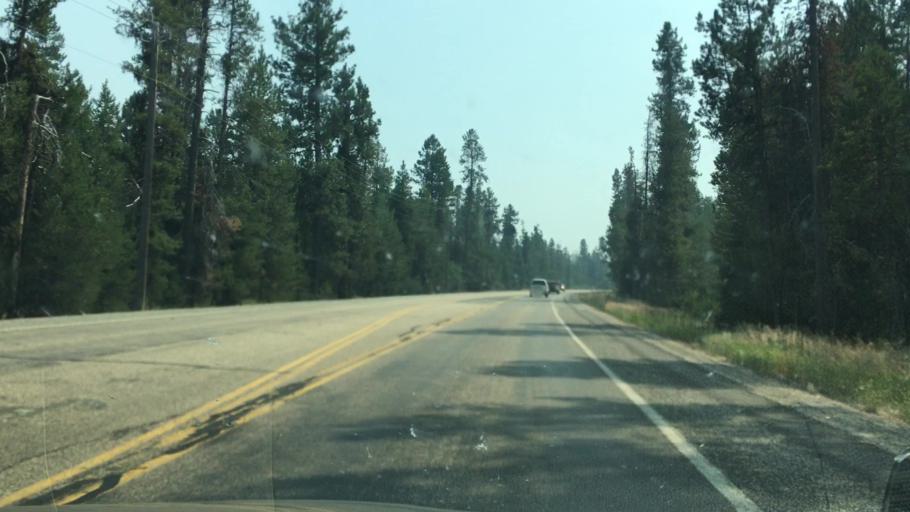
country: US
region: Idaho
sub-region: Valley County
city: Cascade
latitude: 44.4063
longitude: -115.9999
